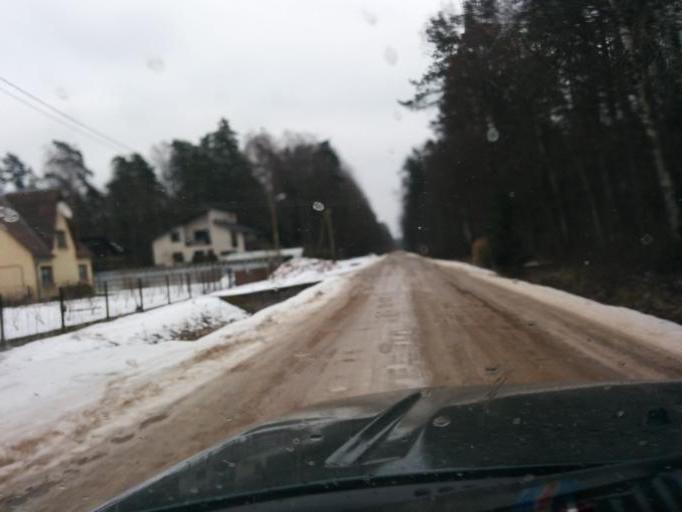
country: LV
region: Ozolnieku
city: Ozolnieki
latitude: 56.6870
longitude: 23.7640
